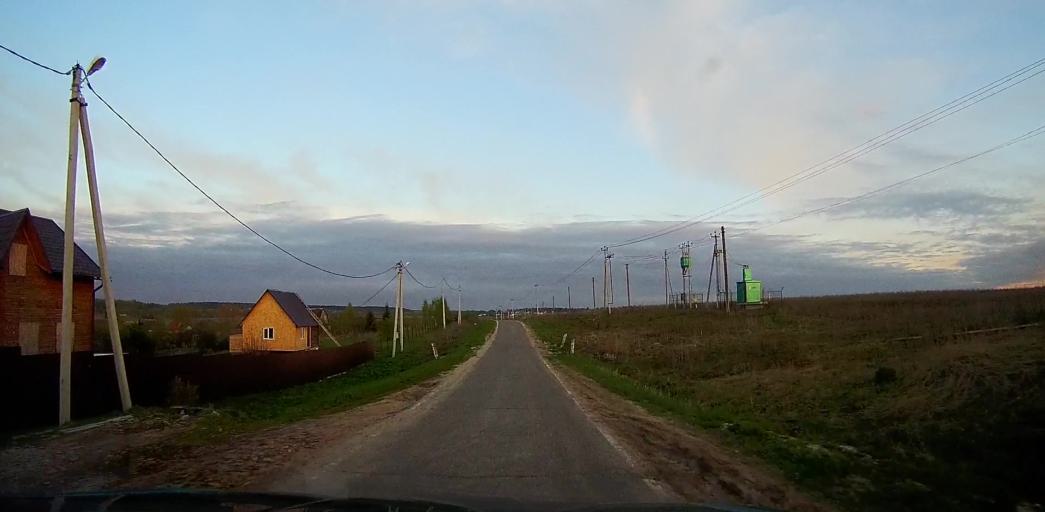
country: RU
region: Moskovskaya
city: Peski
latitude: 55.2281
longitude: 38.7340
